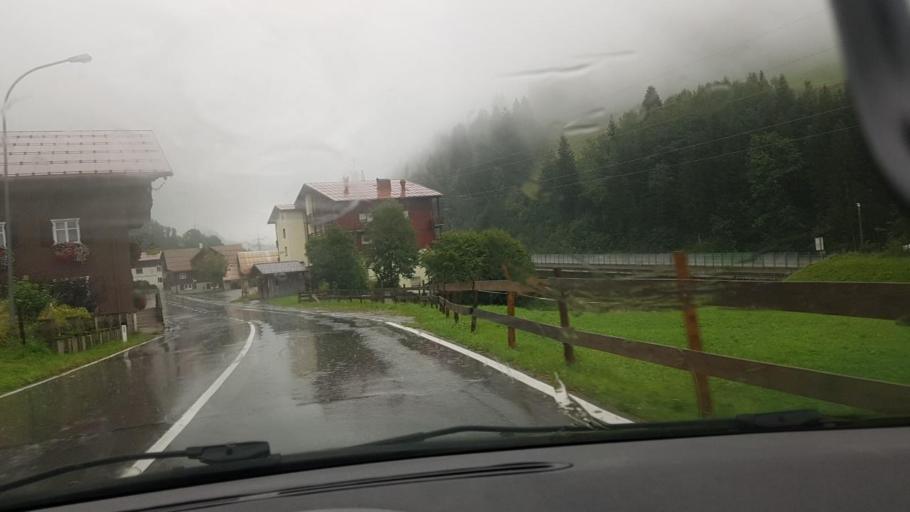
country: AT
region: Vorarlberg
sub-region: Politischer Bezirk Bludenz
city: Klosterle
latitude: 47.1306
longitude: 10.0634
